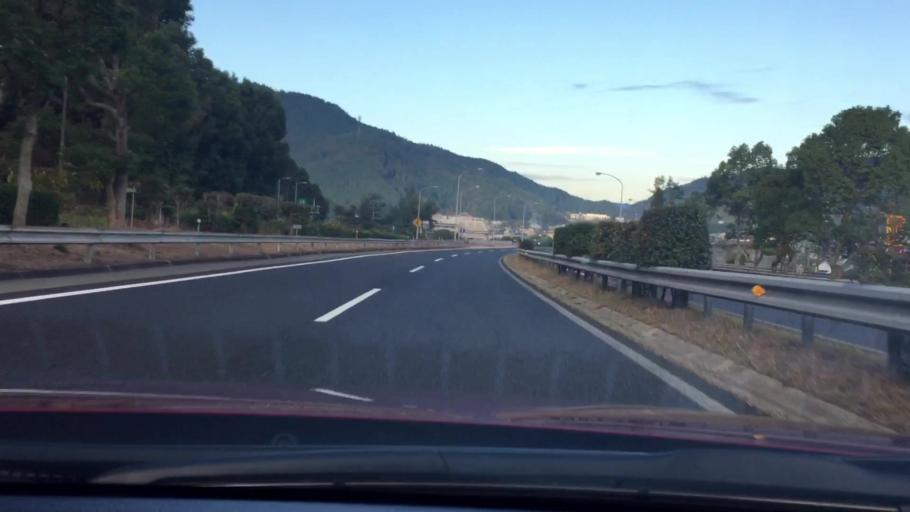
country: JP
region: Hyogo
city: Yamazakicho-nakabirose
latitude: 34.9845
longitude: 134.6034
